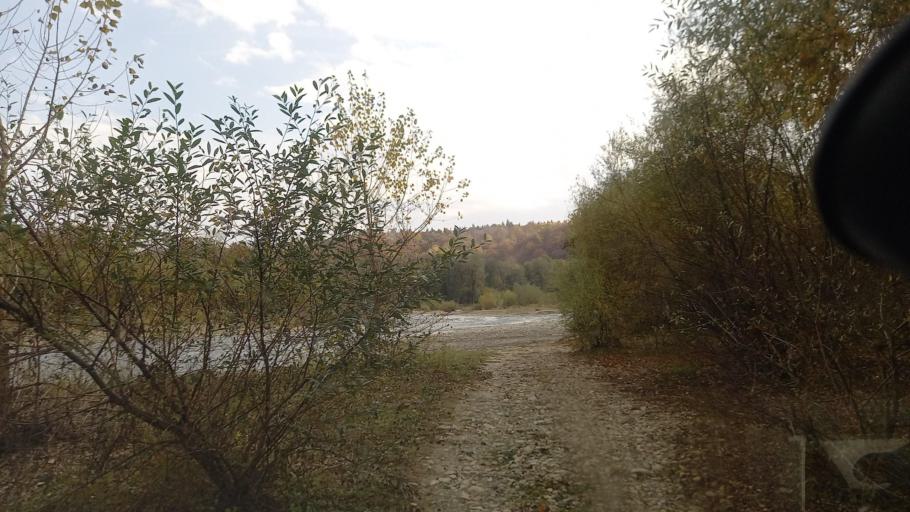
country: RU
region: Krasnodarskiy
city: Shedok
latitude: 44.1696
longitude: 40.8496
